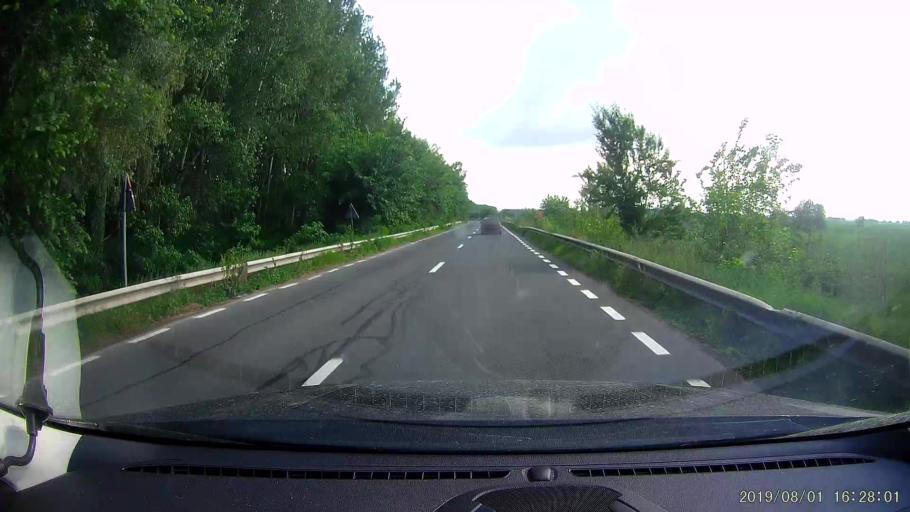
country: RO
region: Calarasi
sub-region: Municipiul Calarasi
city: Calarasi
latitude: 44.1548
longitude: 27.3152
